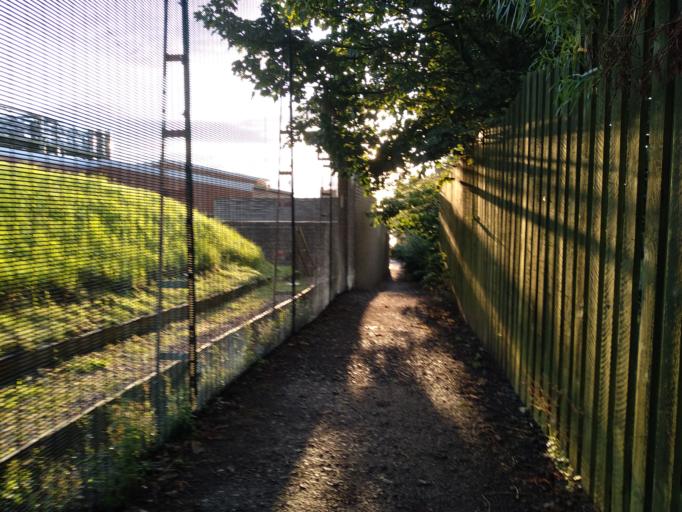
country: GB
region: Scotland
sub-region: Angus
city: Montrose
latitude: 56.7078
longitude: -2.4522
